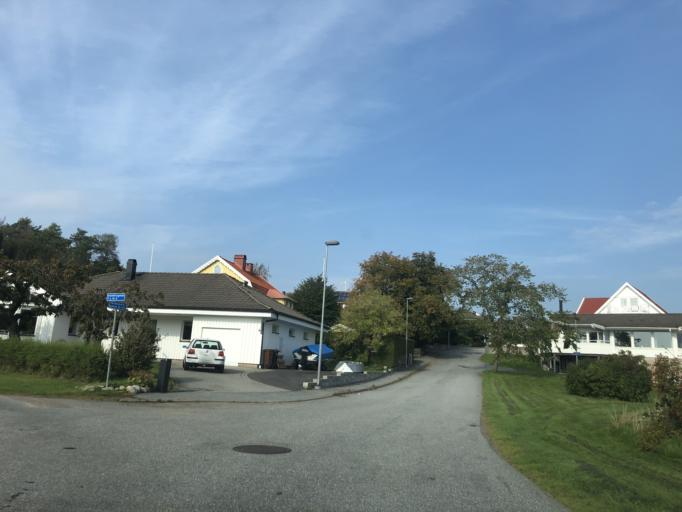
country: SE
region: Vaestra Goetaland
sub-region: Goteborg
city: Majorna
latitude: 57.6432
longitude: 11.8779
